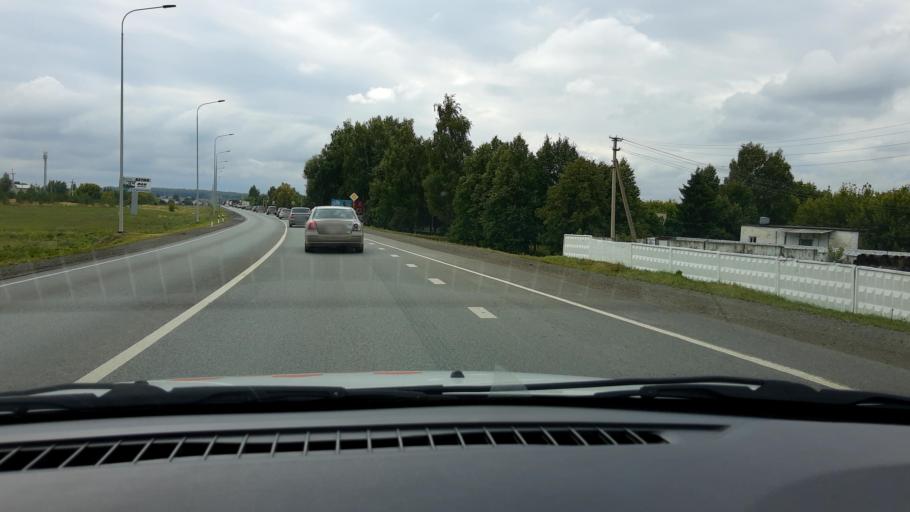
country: RU
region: Tatarstan
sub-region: Alekseyevskiy Rayon
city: Alekseyevskoye
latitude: 55.3057
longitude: 50.1335
